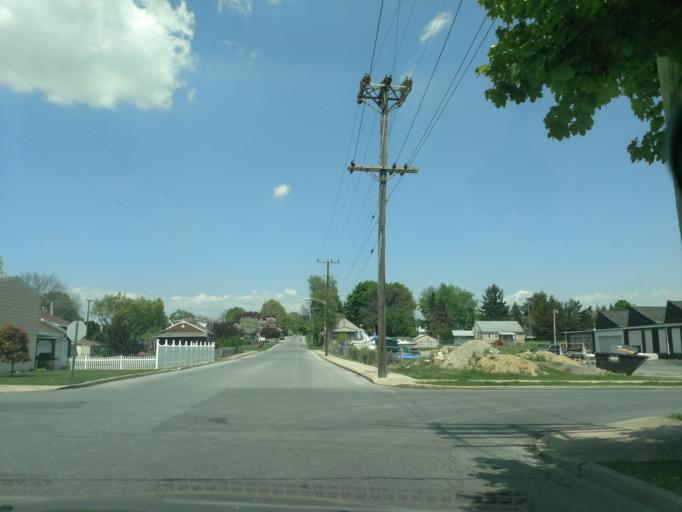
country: US
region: Pennsylvania
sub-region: Lebanon County
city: Lebanon
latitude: 40.3474
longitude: -76.4043
